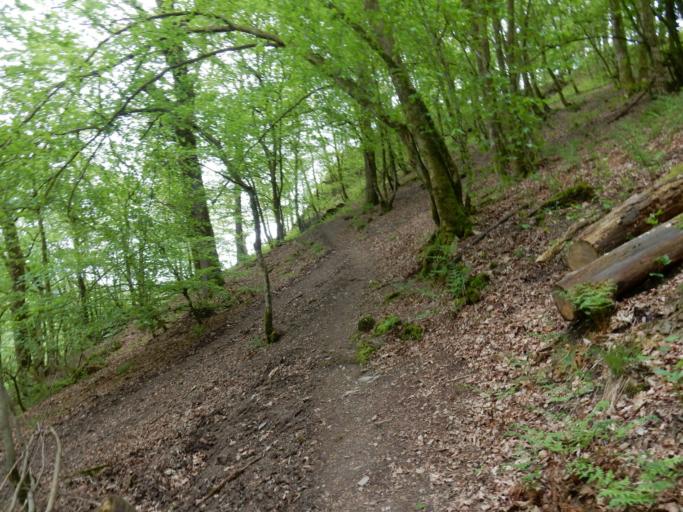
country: BE
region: Wallonia
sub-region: Province du Luxembourg
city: Bouillon
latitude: 49.7932
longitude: 5.0391
